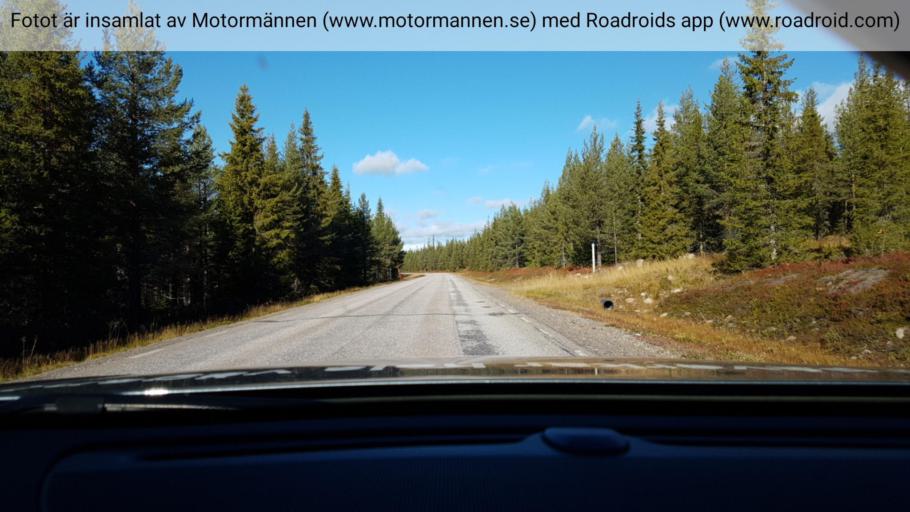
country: SE
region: Norrbotten
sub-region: Arjeplogs Kommun
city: Arjeplog
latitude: 65.8075
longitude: 18.4615
